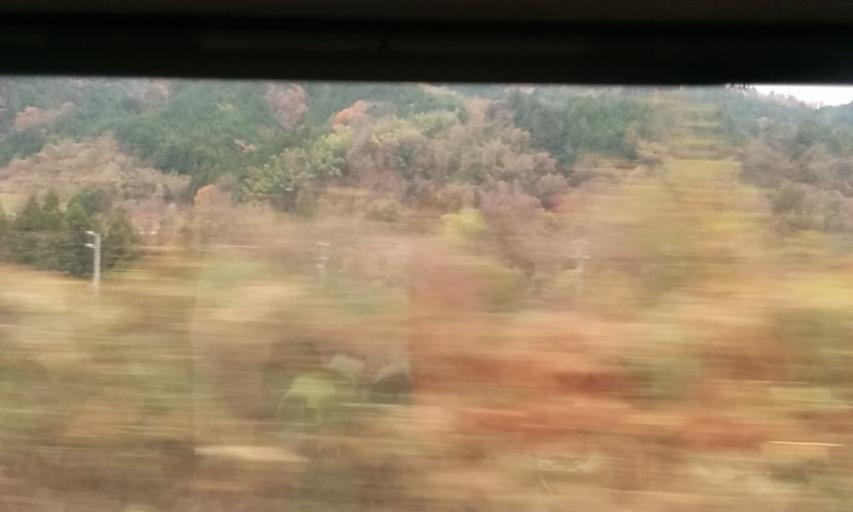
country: JP
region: Gifu
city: Nakatsugawa
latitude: 35.5871
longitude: 137.5410
